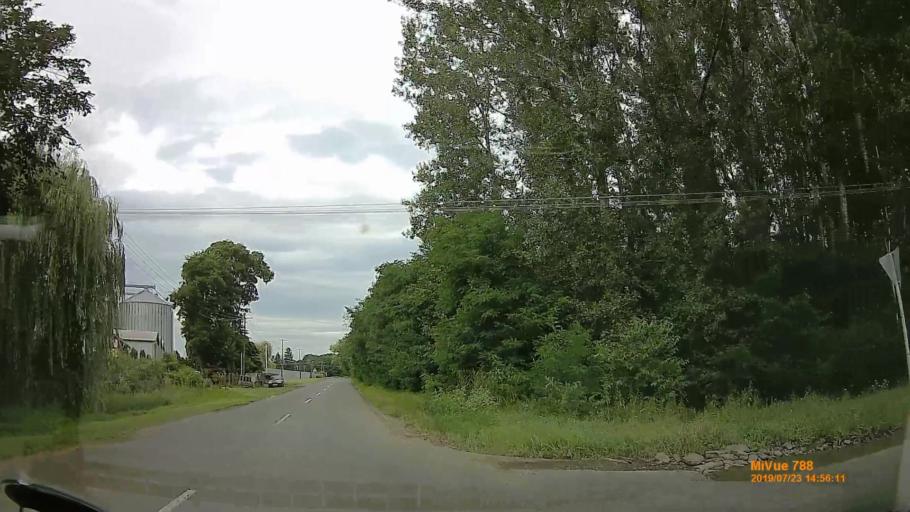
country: HU
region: Szabolcs-Szatmar-Bereg
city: Nyiregyhaza
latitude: 47.8970
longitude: 21.6635
